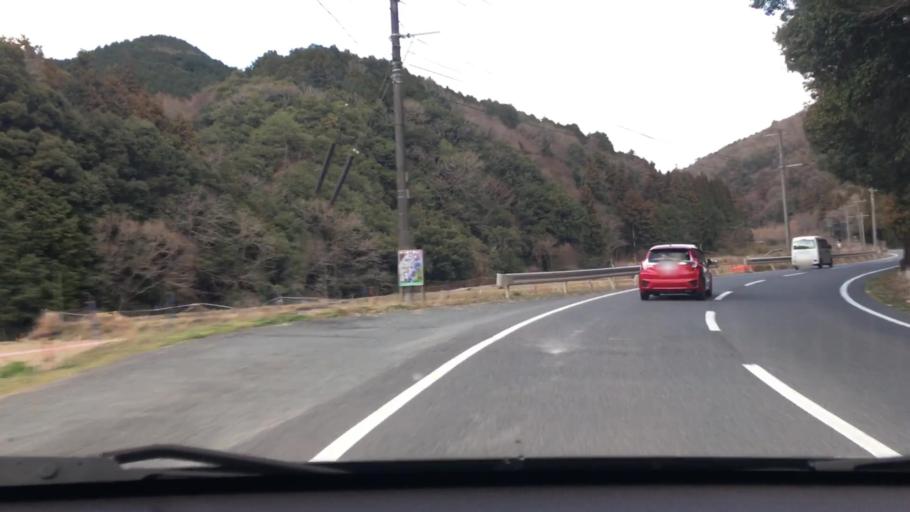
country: JP
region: Oita
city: Bungo-Takada-shi
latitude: 33.4523
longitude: 131.3925
